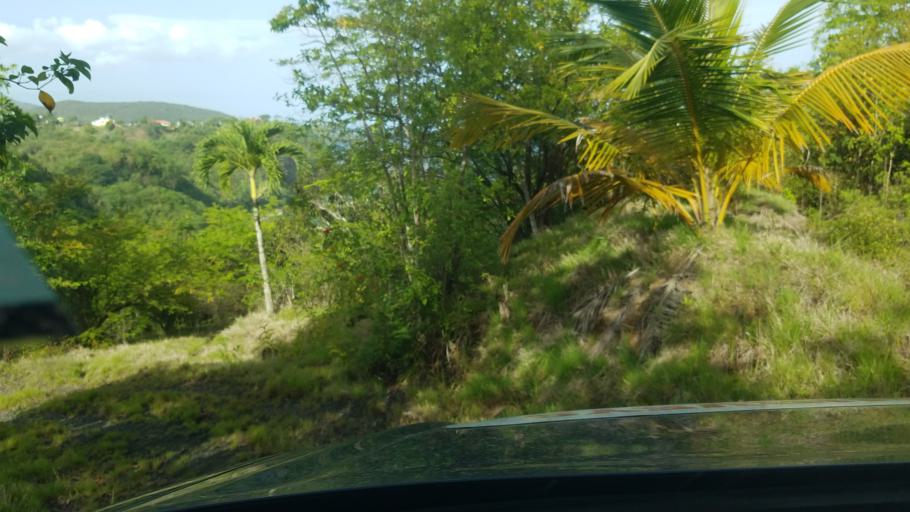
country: LC
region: Anse-la-Raye
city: Anse La Raye
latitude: 13.9522
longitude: -61.0383
